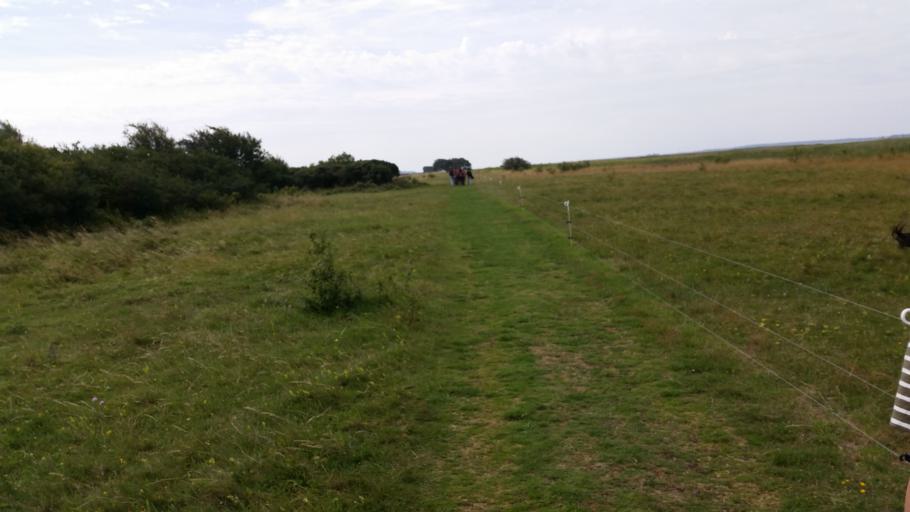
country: DE
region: Mecklenburg-Vorpommern
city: Hiddensee
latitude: 54.5919
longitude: 13.1412
